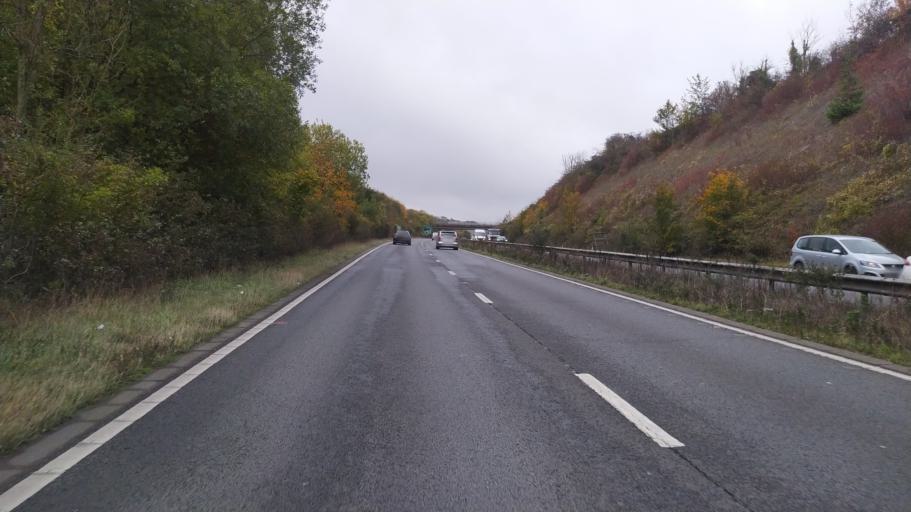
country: GB
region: England
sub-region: Hampshire
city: Cowplain
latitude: 50.9523
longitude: -0.9817
